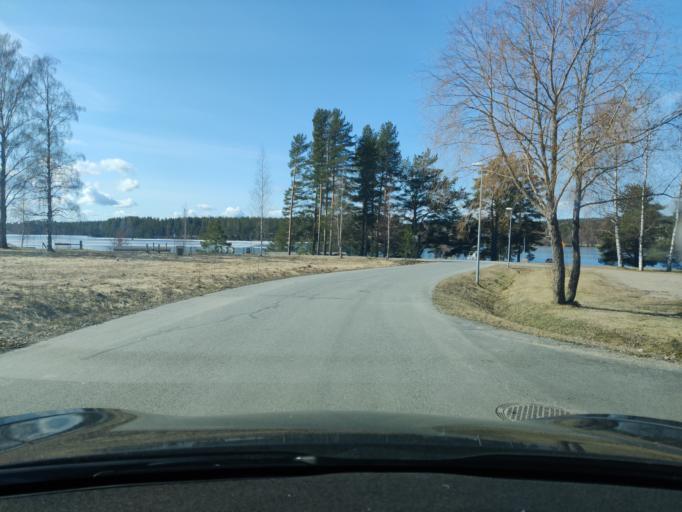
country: FI
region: Northern Savo
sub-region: Kuopio
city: Vehmersalmi
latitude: 62.7635
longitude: 28.0186
